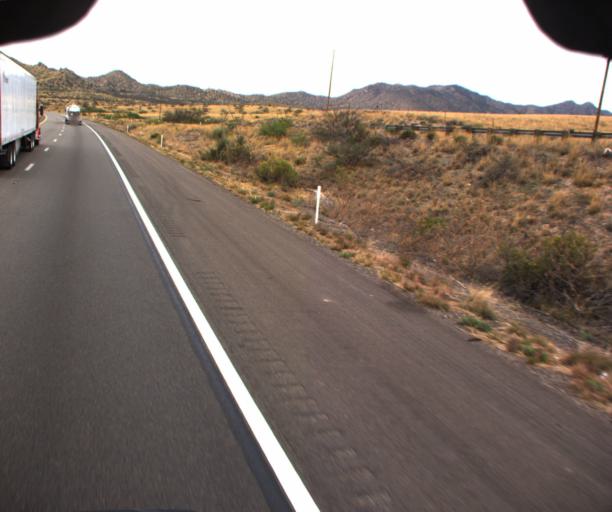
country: US
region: Arizona
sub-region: Cochise County
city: Saint David
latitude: 32.0814
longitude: -110.0530
